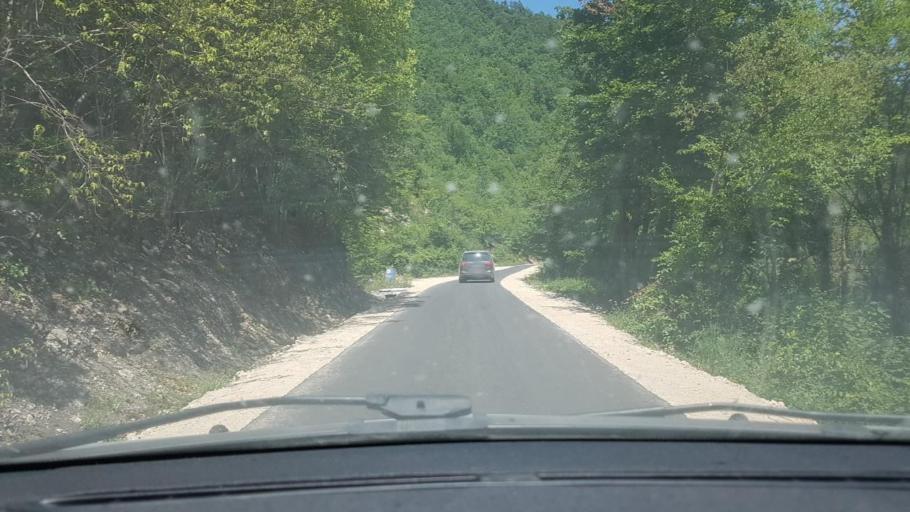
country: BA
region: Federation of Bosnia and Herzegovina
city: Orasac
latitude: 44.6253
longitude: 16.0496
